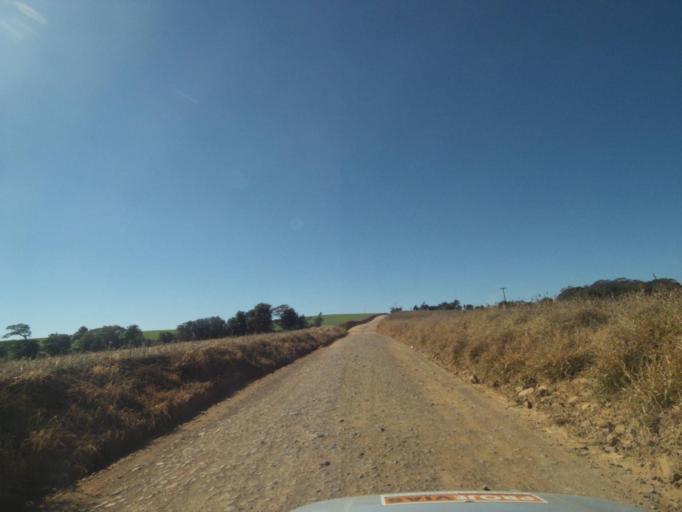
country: BR
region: Parana
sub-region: Tibagi
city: Tibagi
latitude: -24.6203
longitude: -50.6131
